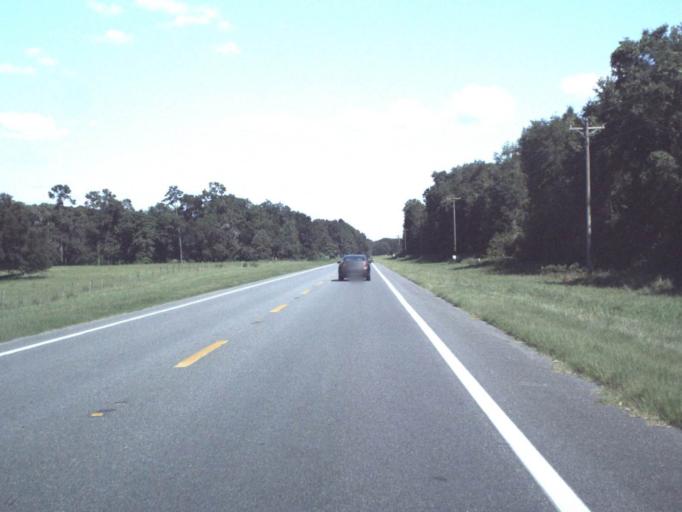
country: US
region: Florida
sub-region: Alachua County
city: High Springs
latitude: 29.8981
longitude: -82.6836
